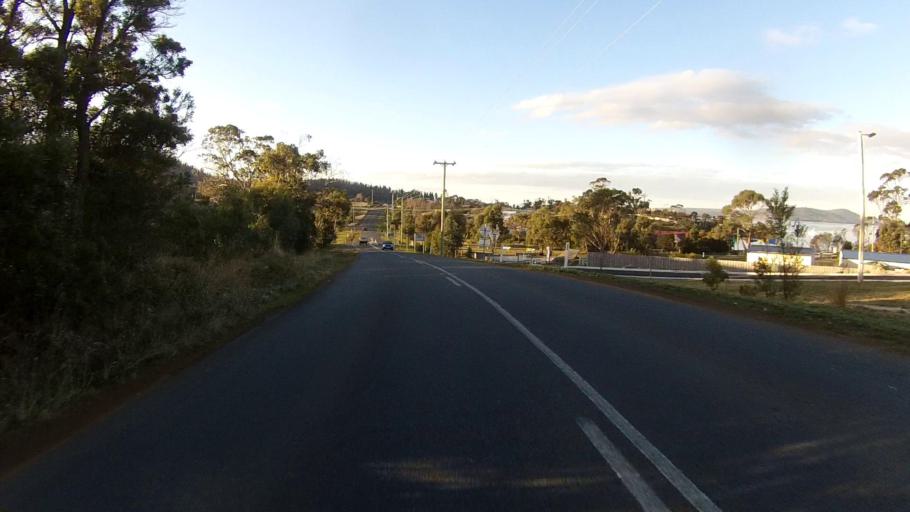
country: AU
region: Tasmania
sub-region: Sorell
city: Sorell
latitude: -42.8866
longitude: 147.8122
